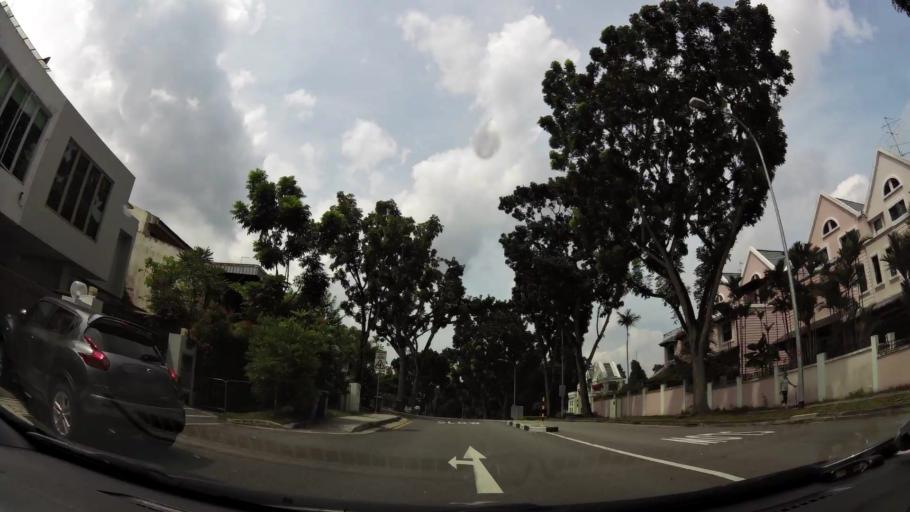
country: SG
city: Singapore
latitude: 1.3397
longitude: 103.7653
